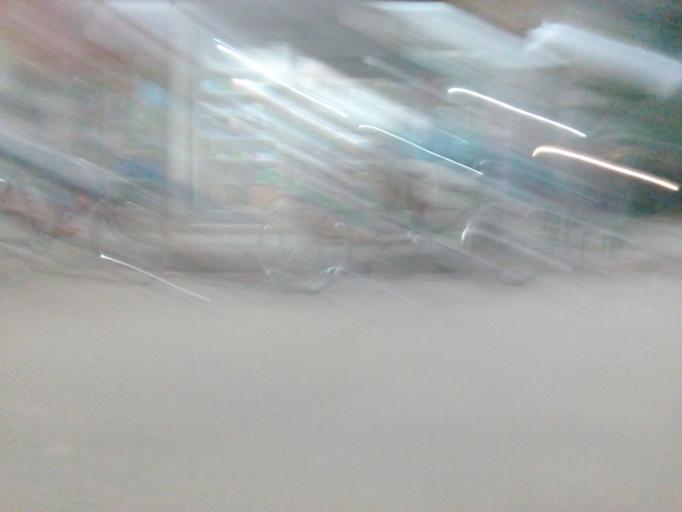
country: BD
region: Dhaka
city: Paltan
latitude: 23.7495
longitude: 90.4283
